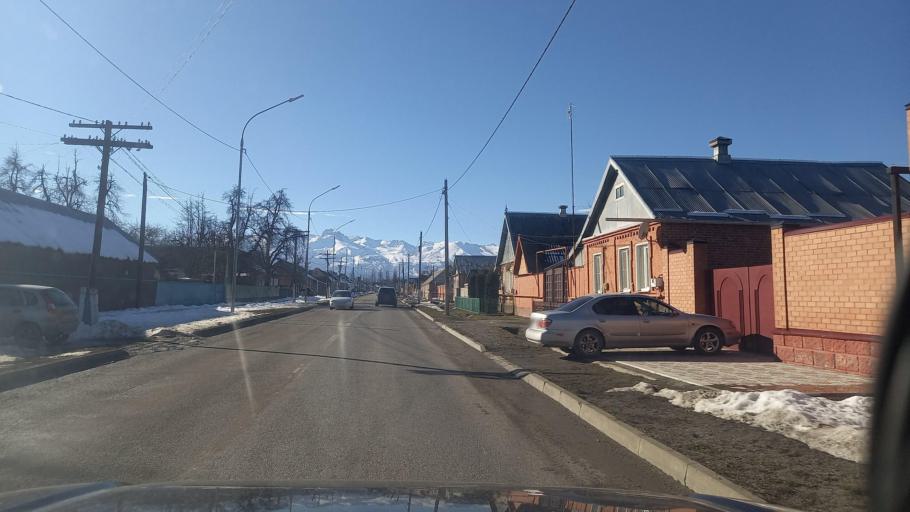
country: RU
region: North Ossetia
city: Chikola
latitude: 43.1907
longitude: 43.9087
